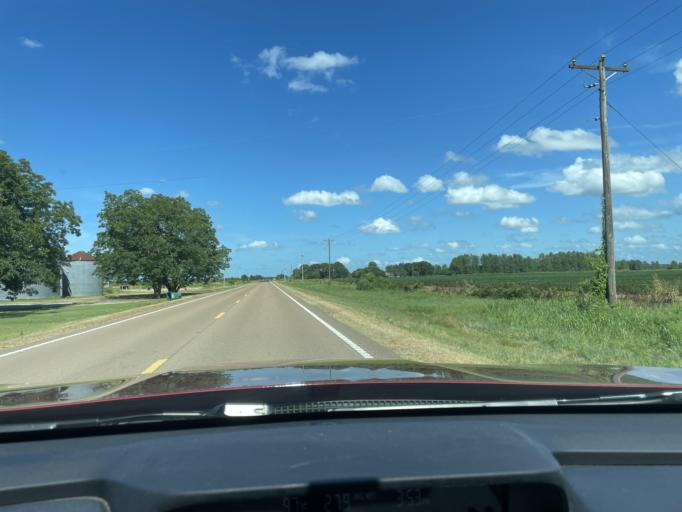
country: US
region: Mississippi
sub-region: Humphreys County
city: Belzoni
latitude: 33.1843
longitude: -90.6712
